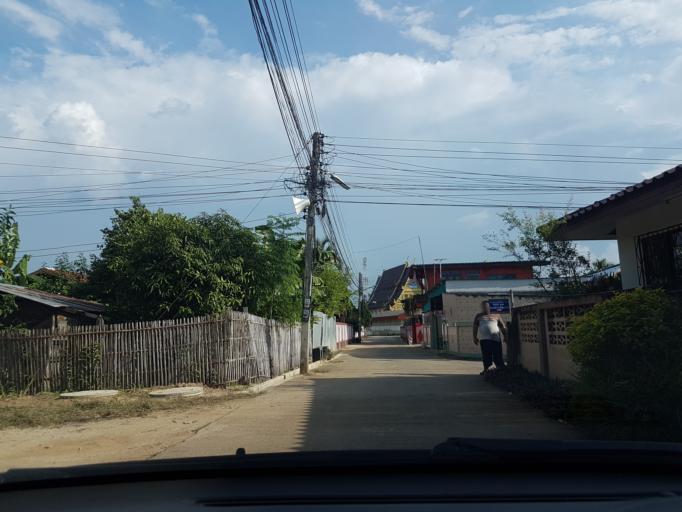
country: TH
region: Lampang
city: Ko Kha
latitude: 18.2185
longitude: 99.4185
